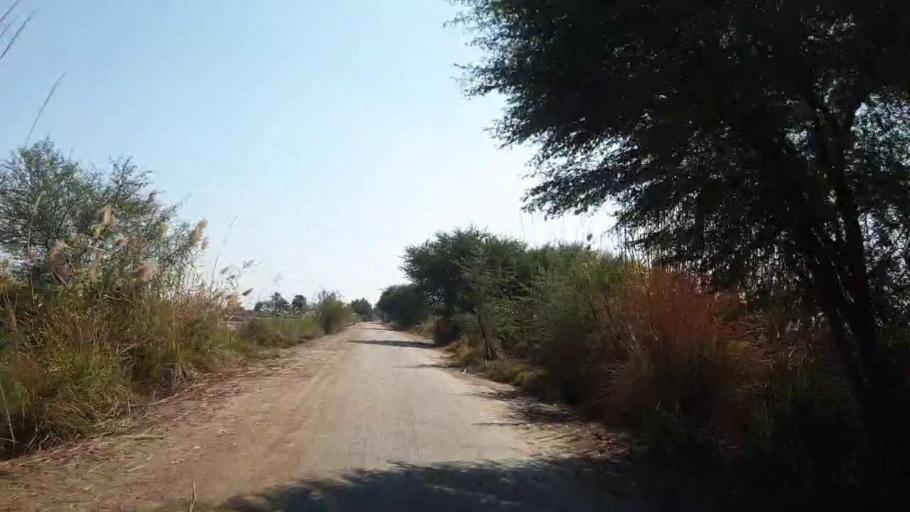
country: PK
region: Sindh
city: Mirpur Khas
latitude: 25.6407
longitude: 69.0279
